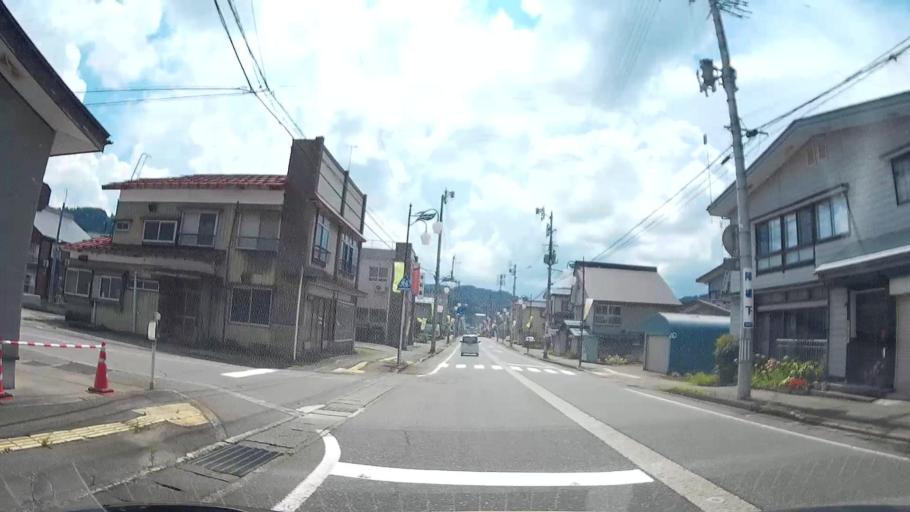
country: JP
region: Niigata
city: Tokamachi
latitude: 37.0164
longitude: 138.6541
